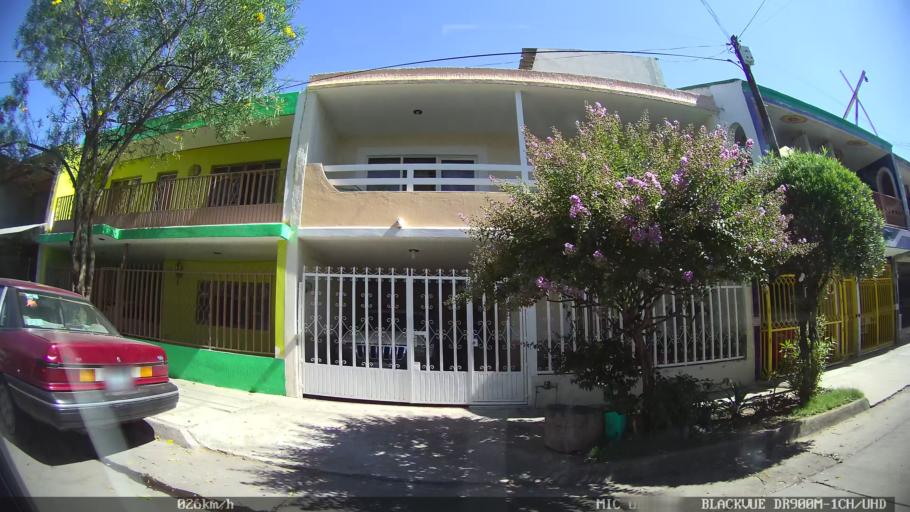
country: MX
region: Jalisco
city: Tlaquepaque
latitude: 20.6567
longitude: -103.2895
